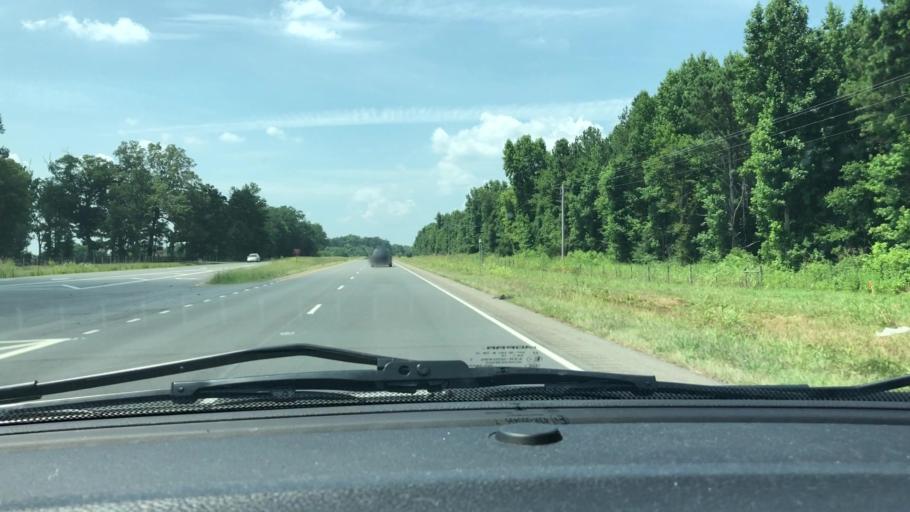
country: US
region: North Carolina
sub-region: Chatham County
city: Siler City
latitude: 35.6618
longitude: -79.4023
